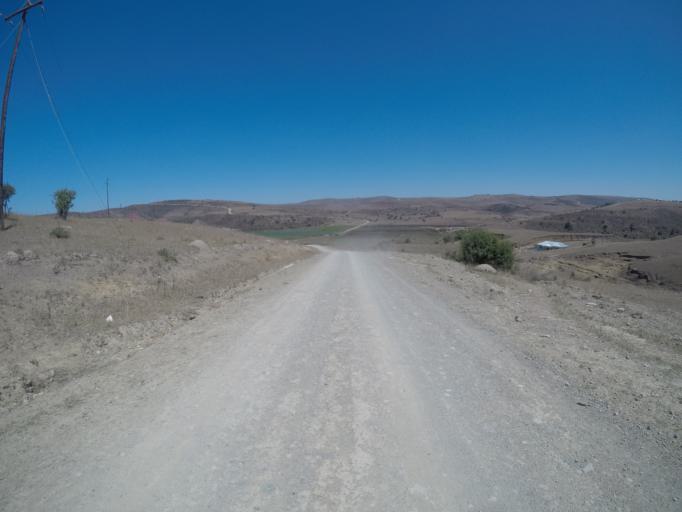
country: ZA
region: Eastern Cape
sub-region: OR Tambo District Municipality
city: Mthatha
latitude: -31.8654
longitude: 28.8723
